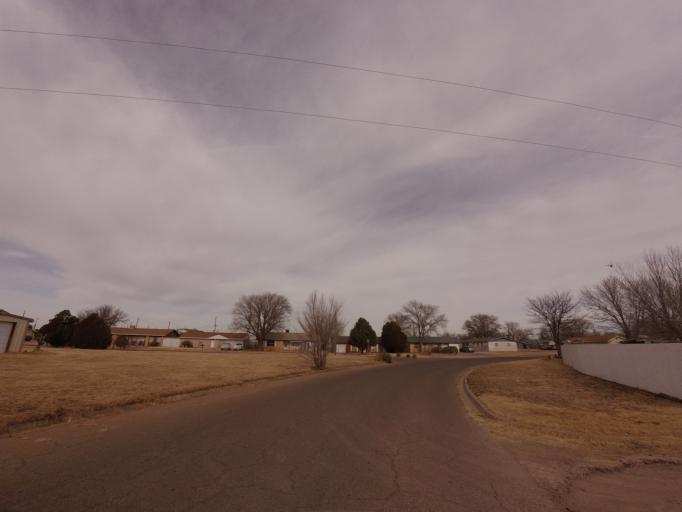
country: US
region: New Mexico
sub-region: Curry County
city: Clovis
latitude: 34.4085
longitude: -103.2456
